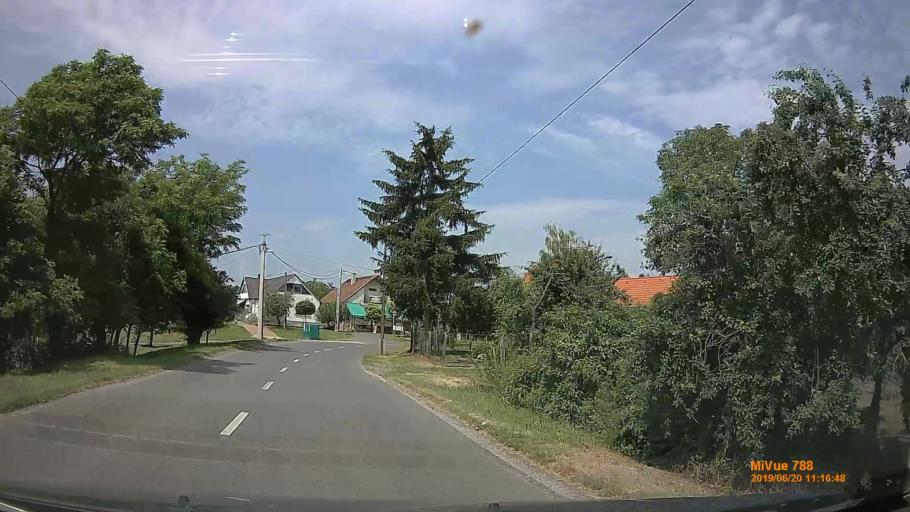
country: HU
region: Baranya
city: Pecsvarad
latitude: 46.1549
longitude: 18.4754
